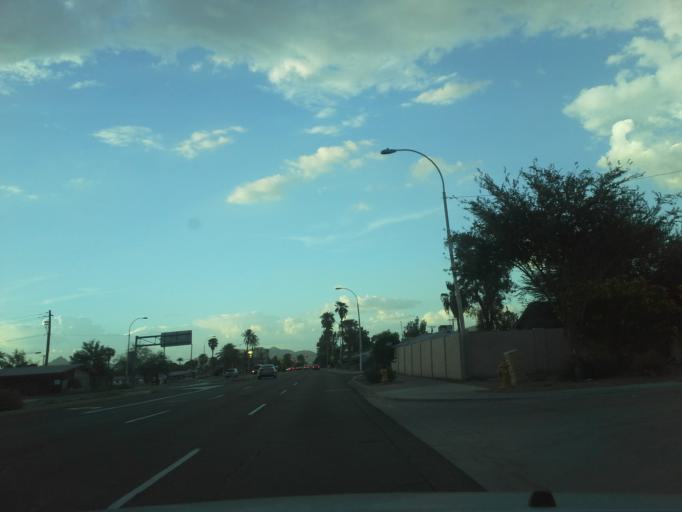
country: US
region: Arizona
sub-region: Maricopa County
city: Tempe Junction
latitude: 33.4666
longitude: -111.9870
